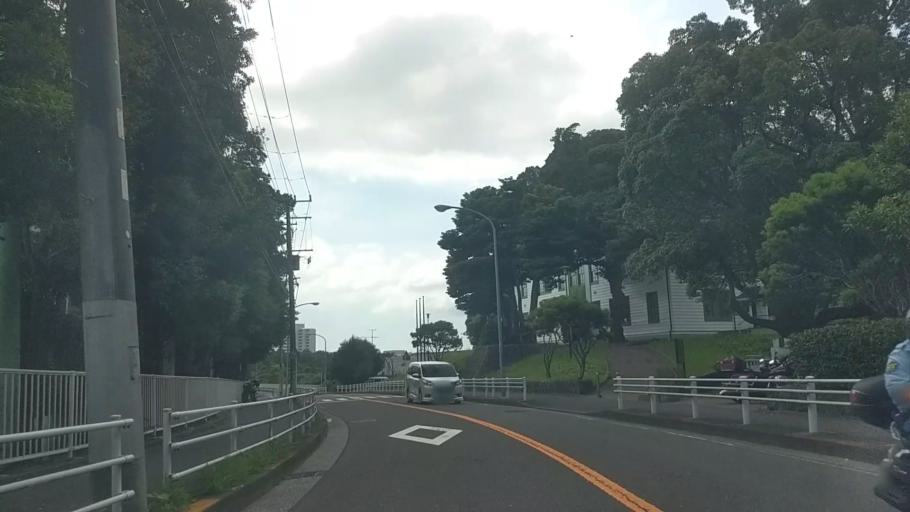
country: JP
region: Kanagawa
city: Yokosuka
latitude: 35.3579
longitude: 139.6363
